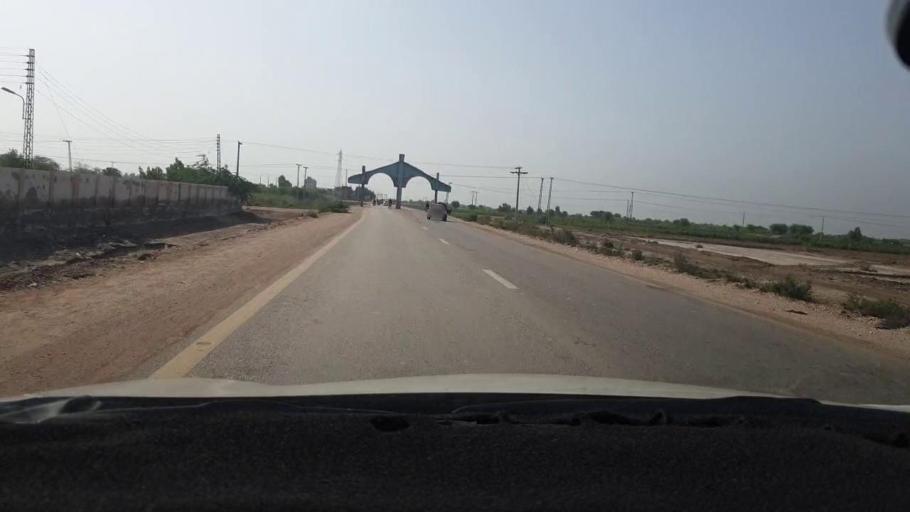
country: PK
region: Sindh
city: Sanghar
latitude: 26.0295
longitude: 68.9534
